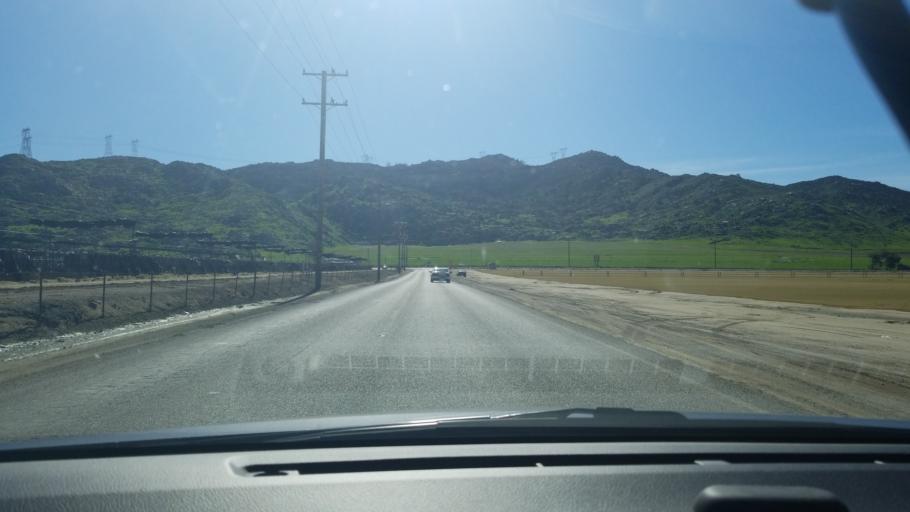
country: US
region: California
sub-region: Riverside County
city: Lakeview
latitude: 33.8430
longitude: -117.0686
